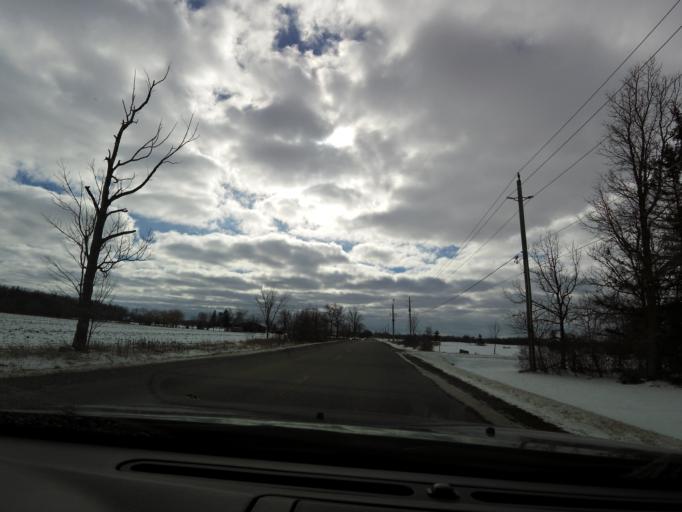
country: CA
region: Ontario
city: Hamilton
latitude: 43.1293
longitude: -79.6524
